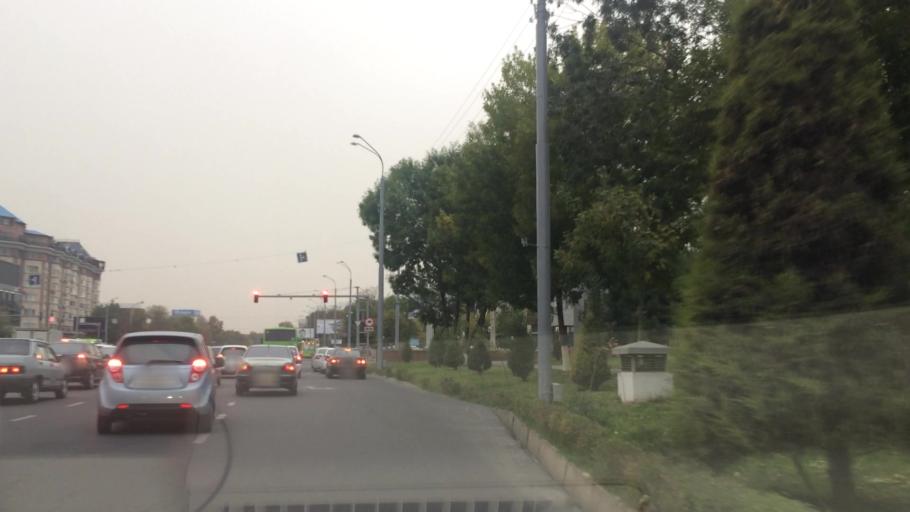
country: UZ
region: Toshkent Shahri
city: Tashkent
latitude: 41.2996
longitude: 69.2740
